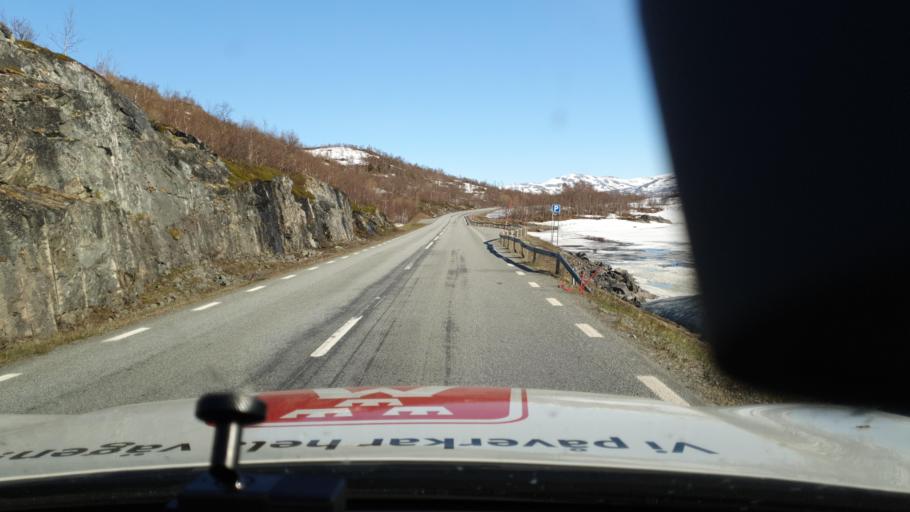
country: NO
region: Nordland
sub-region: Rana
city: Mo i Rana
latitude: 66.1325
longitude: 14.5966
